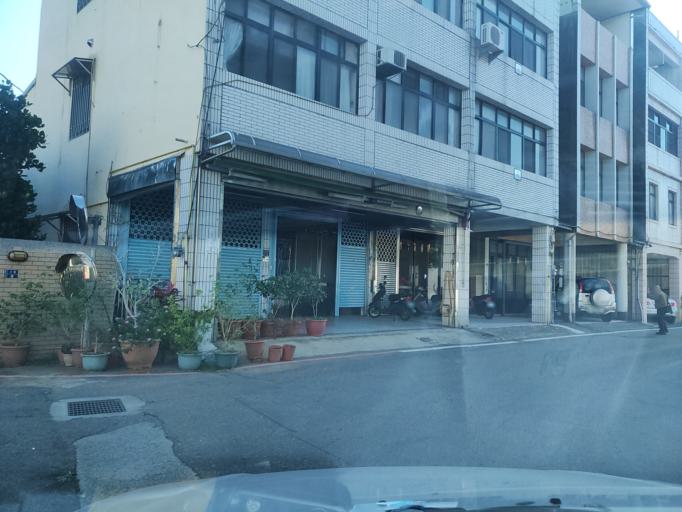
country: TW
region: Taiwan
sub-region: Miaoli
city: Miaoli
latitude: 24.5657
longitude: 120.8256
